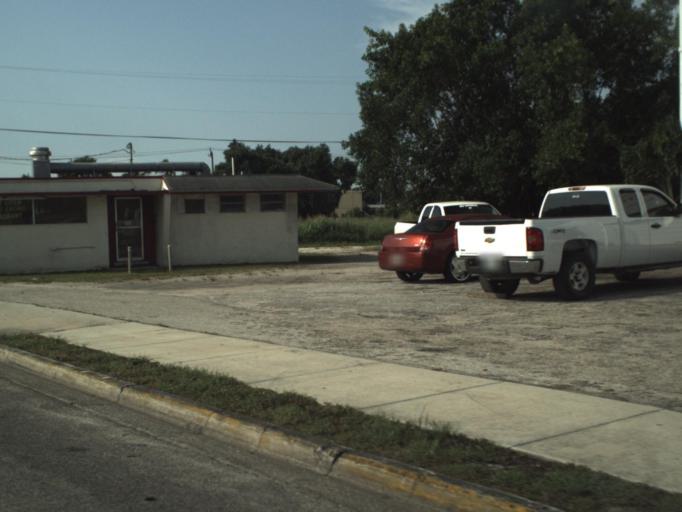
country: US
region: Florida
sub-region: Palm Beach County
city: South Bay
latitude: 26.6690
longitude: -80.7188
